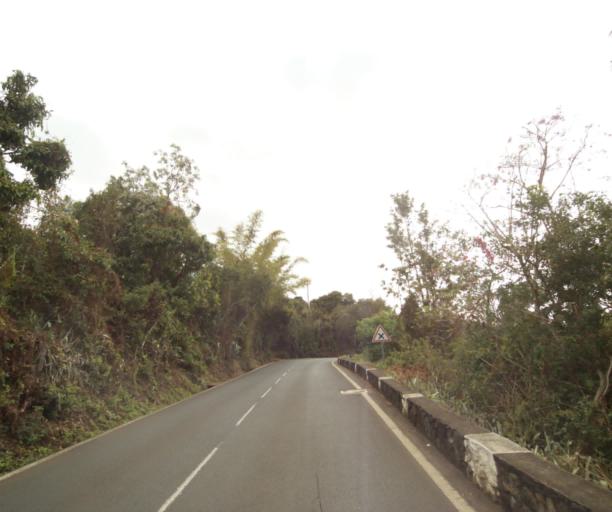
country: RE
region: Reunion
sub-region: Reunion
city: Saint-Paul
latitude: -21.0462
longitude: 55.2879
